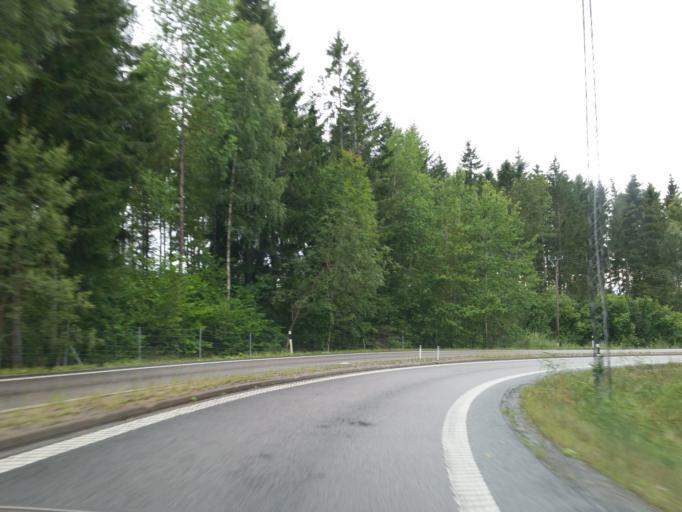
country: SE
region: Uppsala
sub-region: Enkopings Kommun
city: Dalby
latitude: 59.6186
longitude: 17.3925
